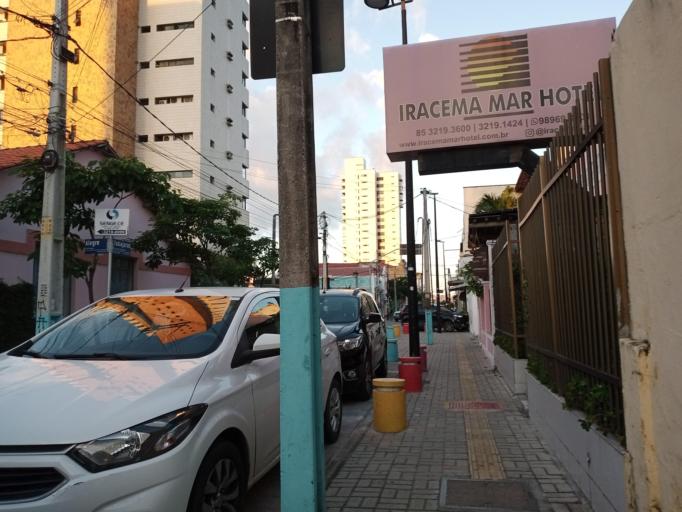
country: BR
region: Ceara
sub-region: Fortaleza
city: Fortaleza
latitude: -3.7196
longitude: -38.5152
